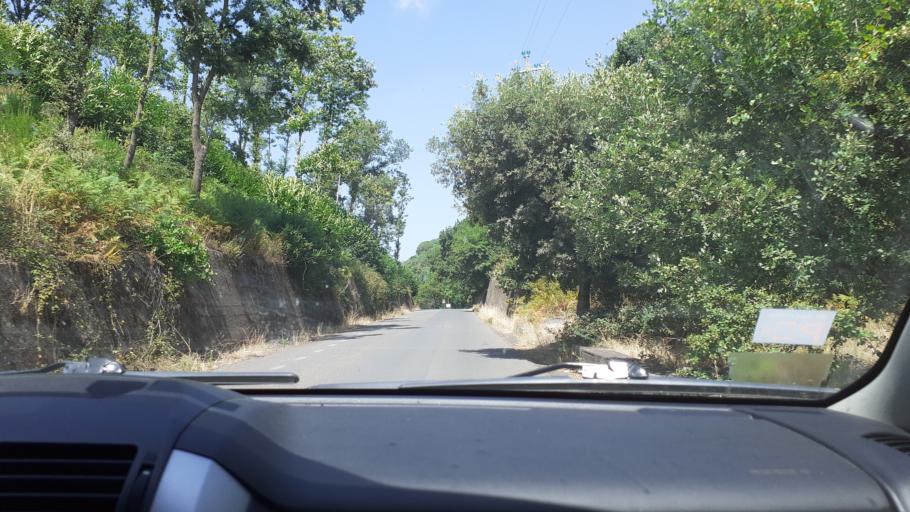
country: IT
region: Sicily
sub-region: Catania
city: Nicolosi
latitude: 37.6367
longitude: 15.0235
